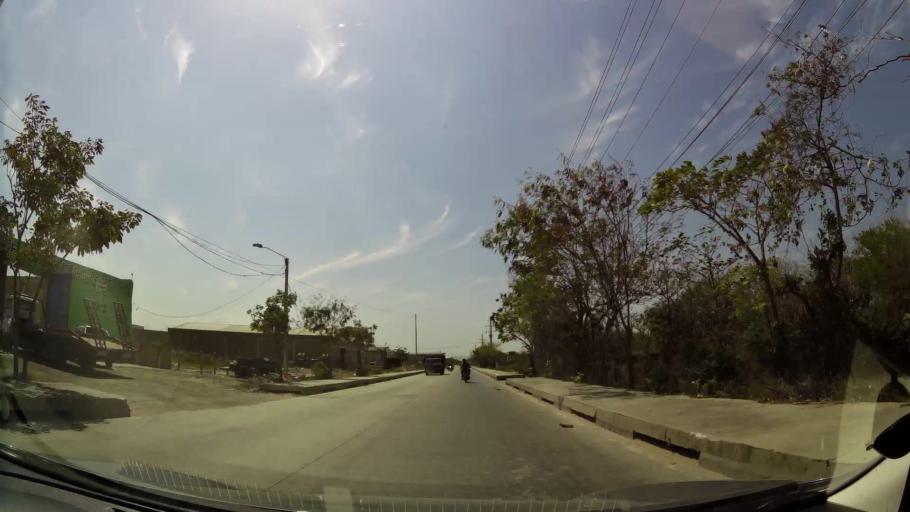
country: CO
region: Atlantico
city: Barranquilla
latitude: 10.9795
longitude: -74.8476
